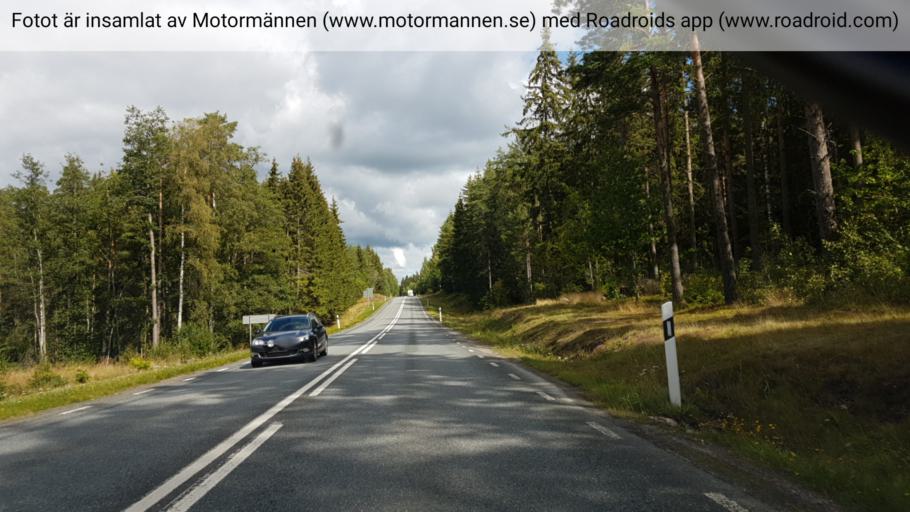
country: SE
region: Joenkoeping
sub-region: Aneby Kommun
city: Aneby
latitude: 57.8893
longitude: 14.8812
